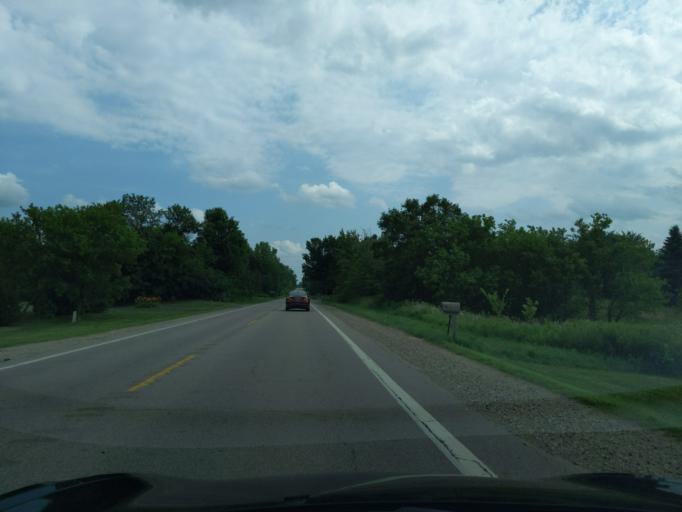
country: US
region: Michigan
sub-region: Eaton County
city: Eaton Rapids
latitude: 42.4338
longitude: -84.6497
